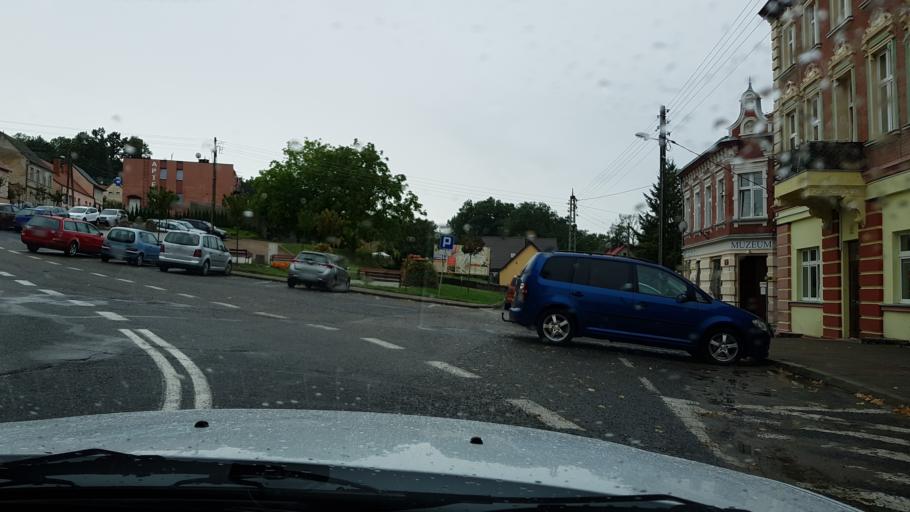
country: PL
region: West Pomeranian Voivodeship
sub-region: Powiat gryfinski
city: Cedynia
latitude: 52.8779
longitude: 14.2029
